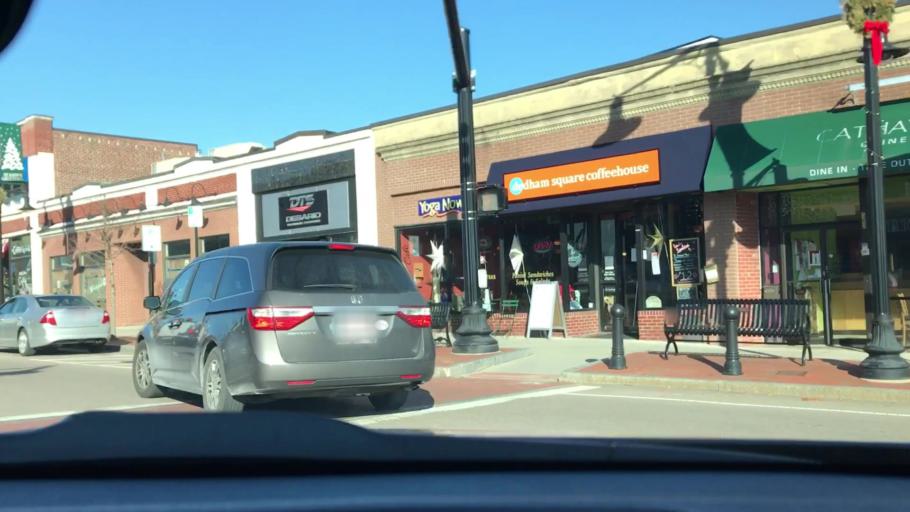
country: US
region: Massachusetts
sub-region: Norfolk County
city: Dedham
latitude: 42.2480
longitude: -71.1726
